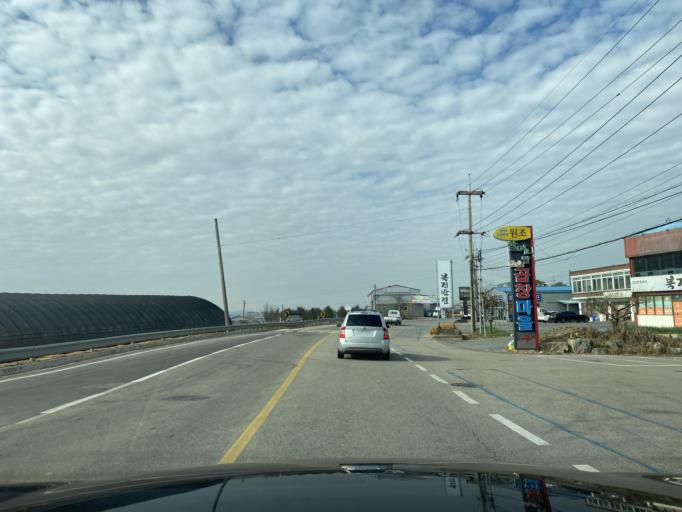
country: KR
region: Chungcheongnam-do
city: Yesan
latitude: 36.6850
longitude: 126.8047
